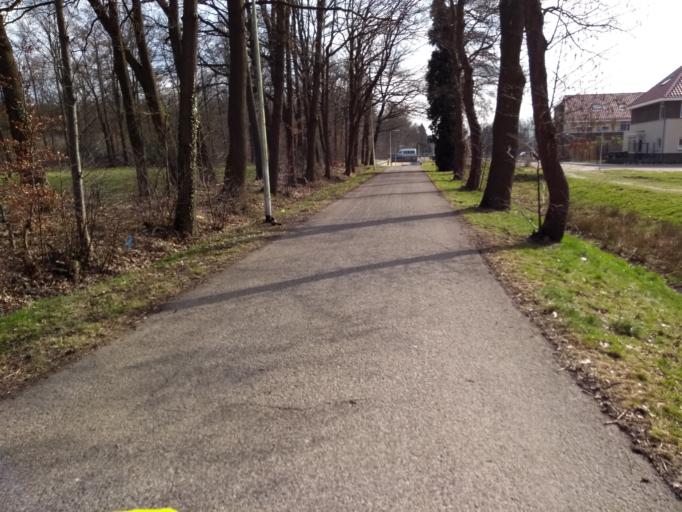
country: NL
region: Overijssel
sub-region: Gemeente Almelo
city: Almelo
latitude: 52.3389
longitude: 6.6679
